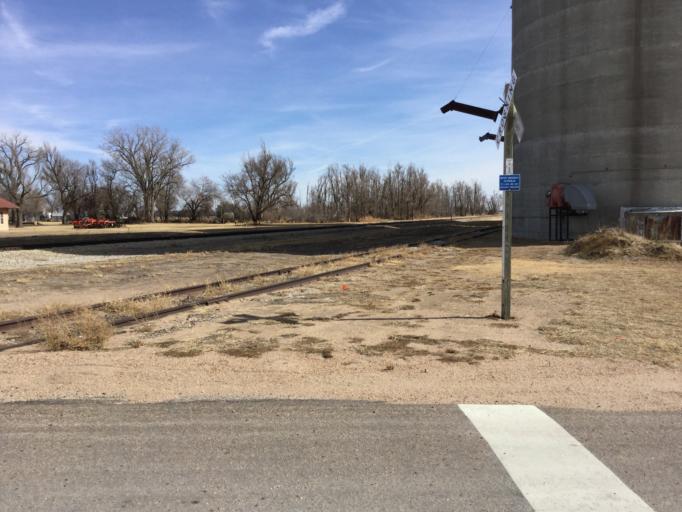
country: US
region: Kansas
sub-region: Rice County
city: Sterling
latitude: 38.2420
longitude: -98.3121
